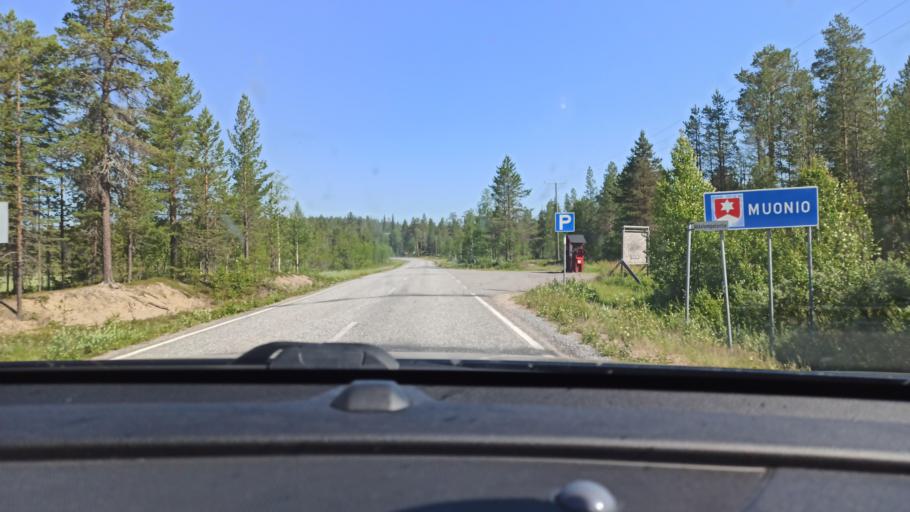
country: FI
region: Lapland
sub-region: Tunturi-Lappi
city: Kolari
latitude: 67.6316
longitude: 24.1580
